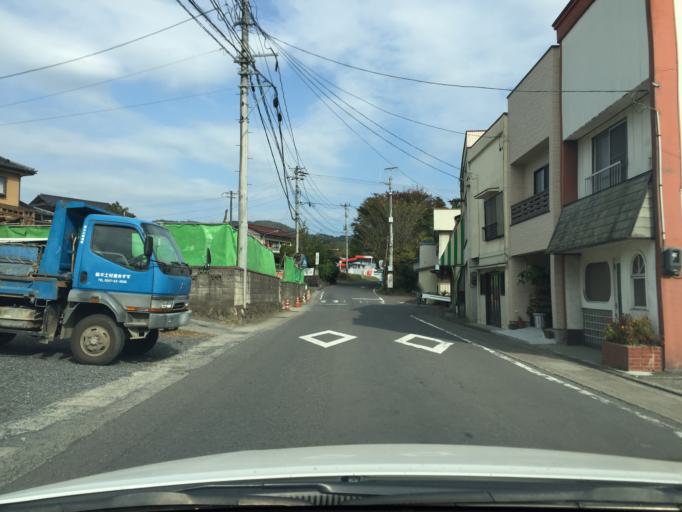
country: JP
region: Fukushima
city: Ishikawa
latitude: 36.9669
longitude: 140.4339
